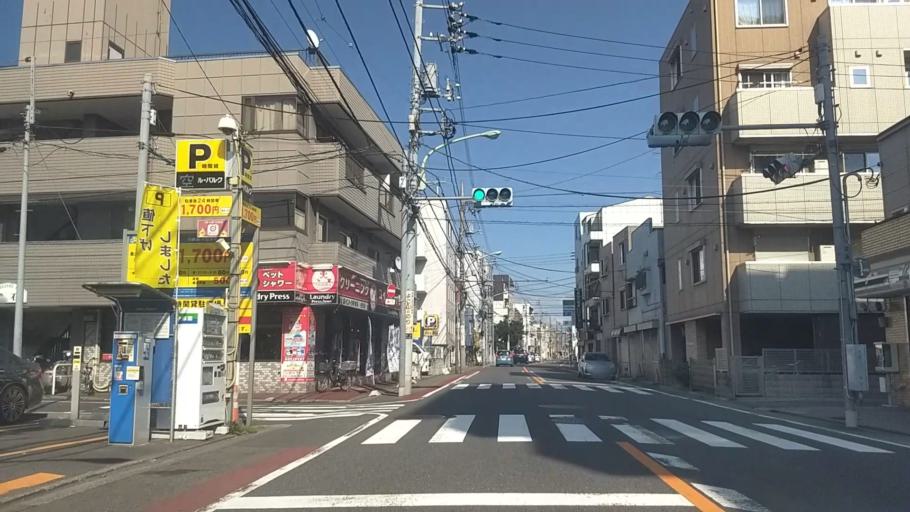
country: JP
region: Kanagawa
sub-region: Kawasaki-shi
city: Kawasaki
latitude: 35.5482
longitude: 139.7473
